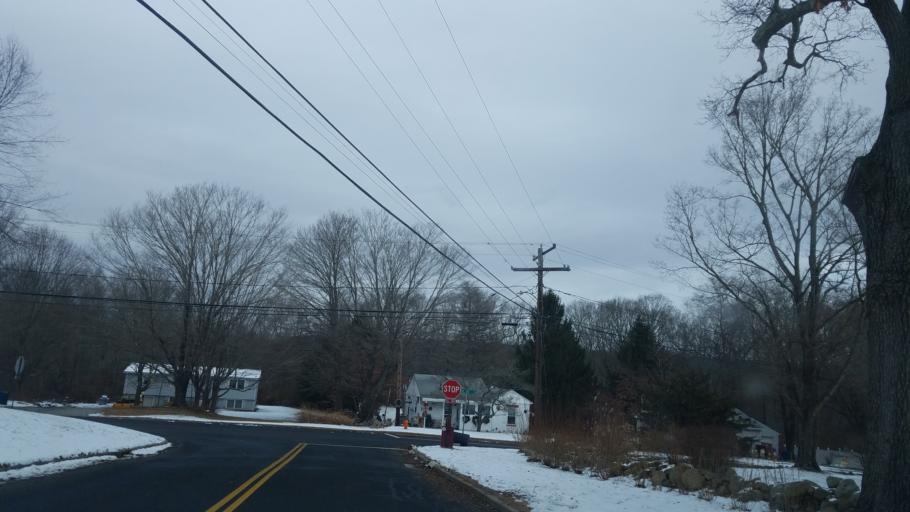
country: US
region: Connecticut
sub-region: New London County
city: Central Waterford
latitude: 41.3470
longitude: -72.1555
